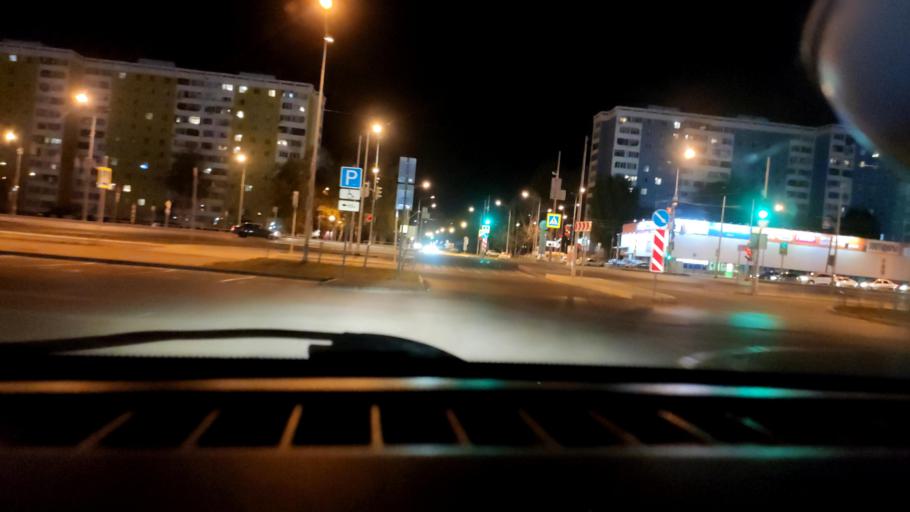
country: RU
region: Samara
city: Samara
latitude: 53.2575
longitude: 50.2346
